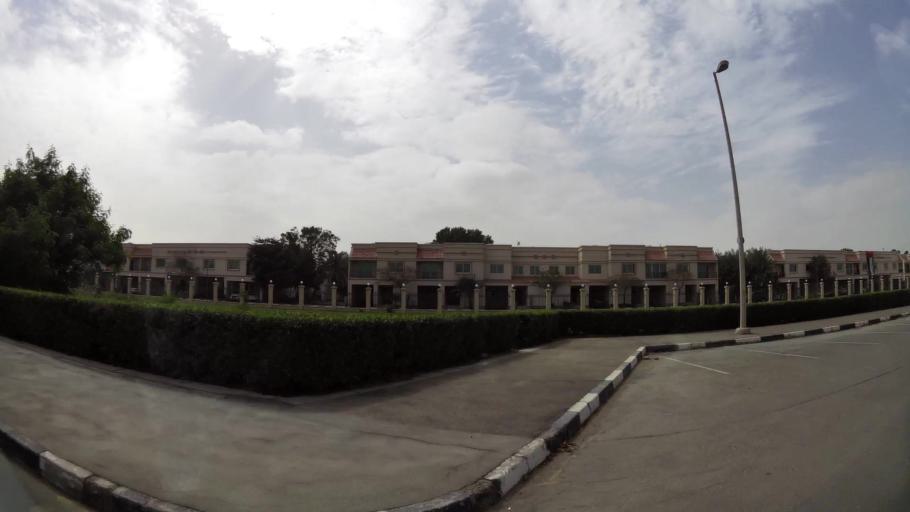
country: AE
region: Abu Dhabi
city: Abu Dhabi
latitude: 24.3928
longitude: 54.4980
